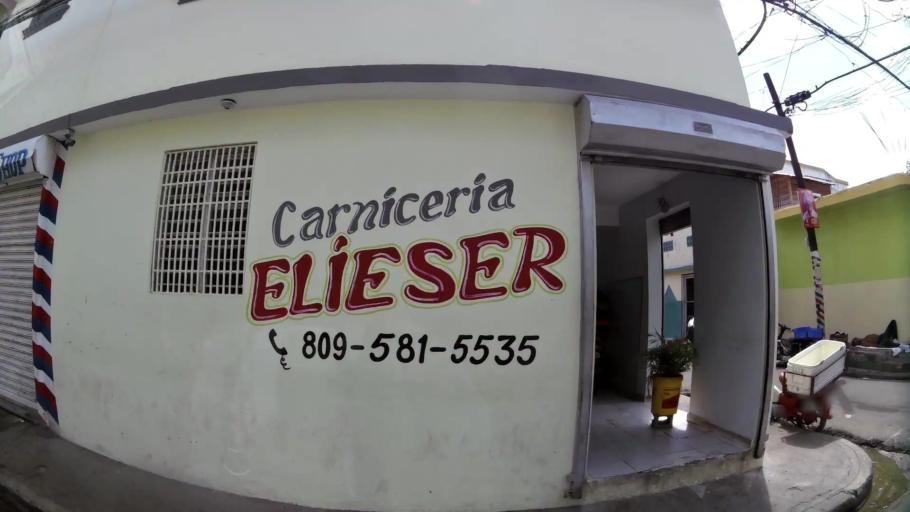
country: DO
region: Santiago
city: Santiago de los Caballeros
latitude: 19.4682
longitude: -70.7017
